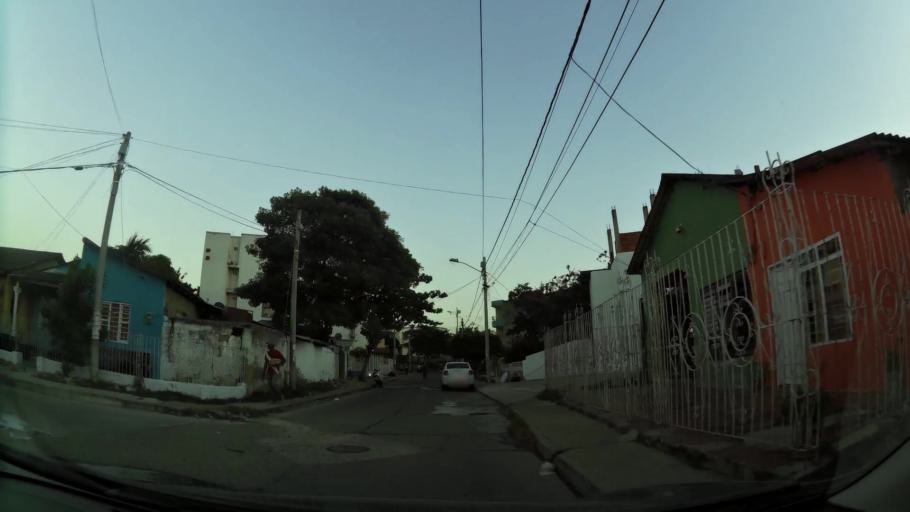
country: CO
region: Bolivar
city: Cartagena
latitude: 10.4035
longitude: -75.5151
